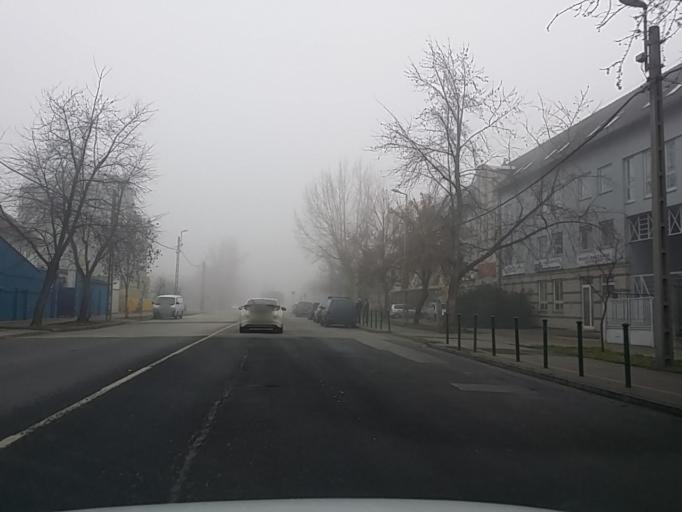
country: HU
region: Budapest
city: Budapest XIII. keruelet
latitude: 47.5388
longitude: 19.0766
